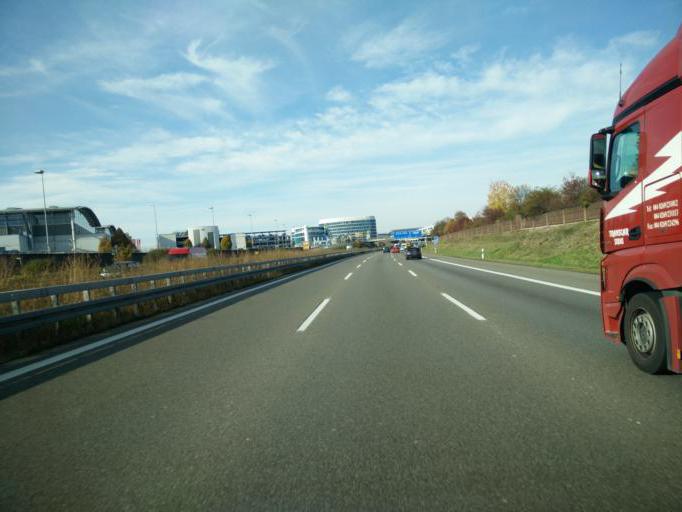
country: DE
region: Baden-Wuerttemberg
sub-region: Regierungsbezirk Stuttgart
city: Leinfelden-Echterdingen
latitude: 48.6925
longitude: 9.2054
